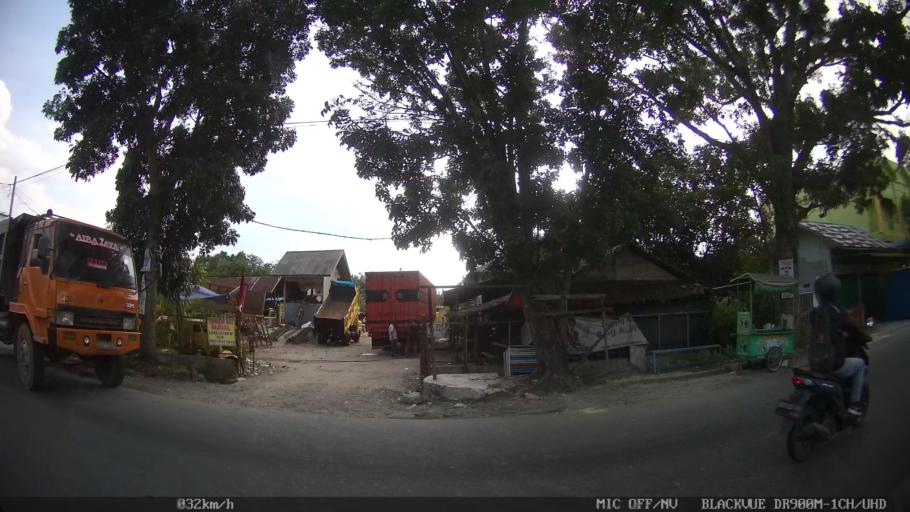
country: ID
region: North Sumatra
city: Binjai
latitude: 3.6344
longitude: 98.4890
